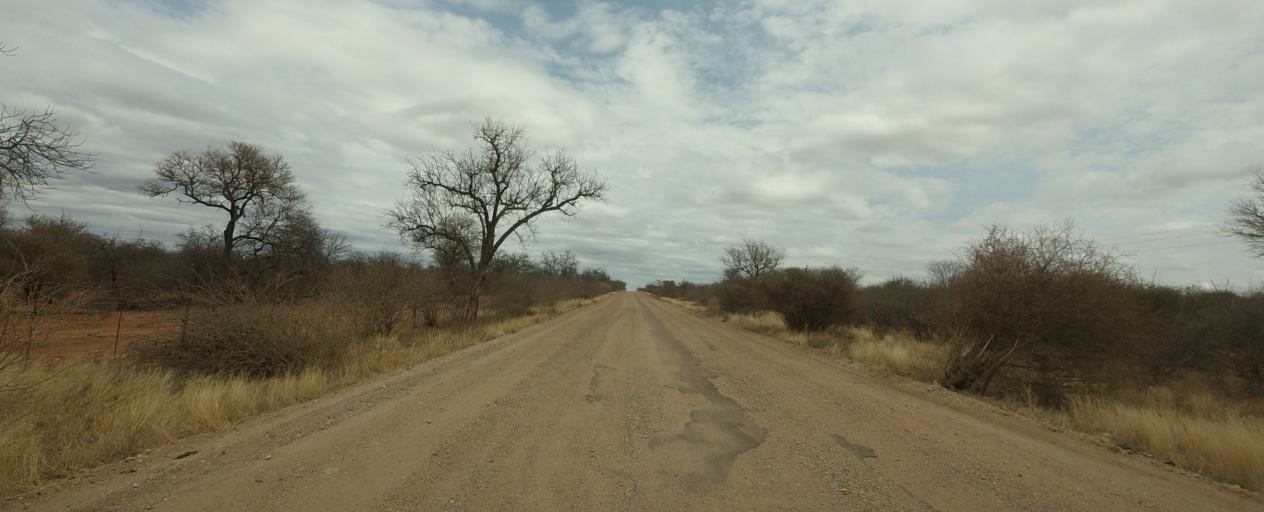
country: BW
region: Central
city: Mathathane
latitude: -22.6704
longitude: 28.6841
